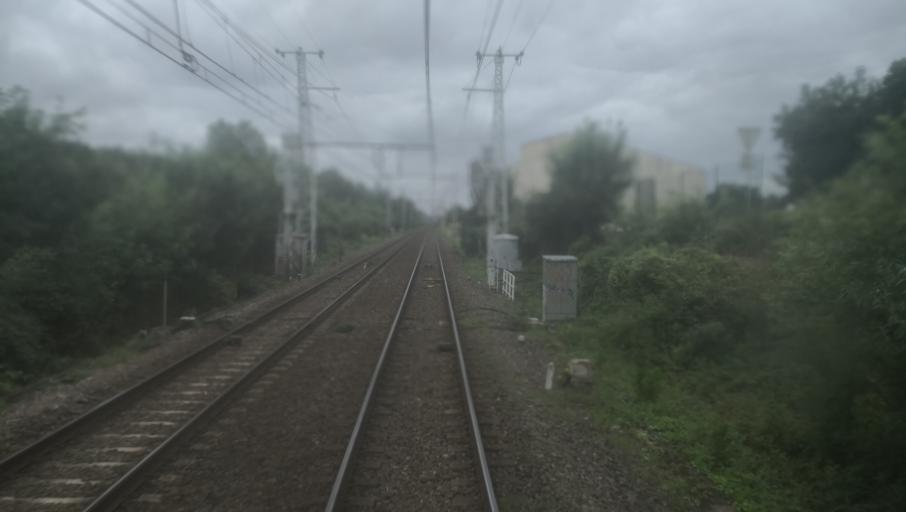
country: FR
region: Midi-Pyrenees
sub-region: Departement de la Haute-Garonne
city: Lespinasse
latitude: 43.7100
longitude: 1.3868
